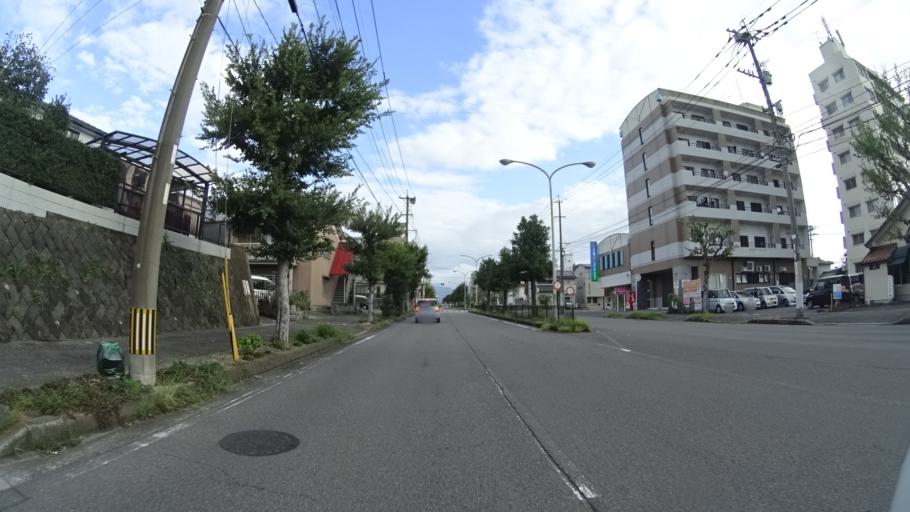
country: JP
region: Oita
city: Beppu
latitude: 33.2925
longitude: 131.4958
